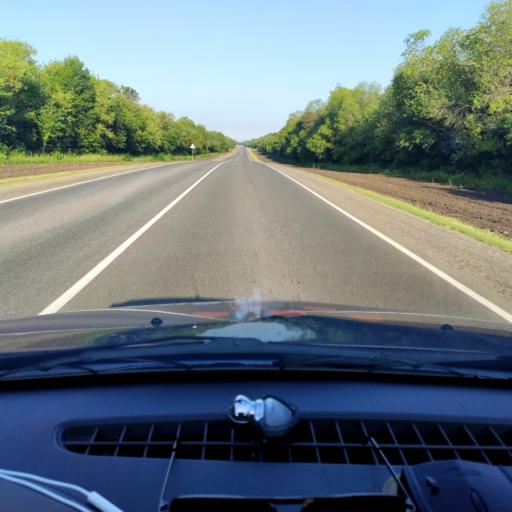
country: RU
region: Orjol
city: Livny
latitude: 52.4256
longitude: 37.7542
